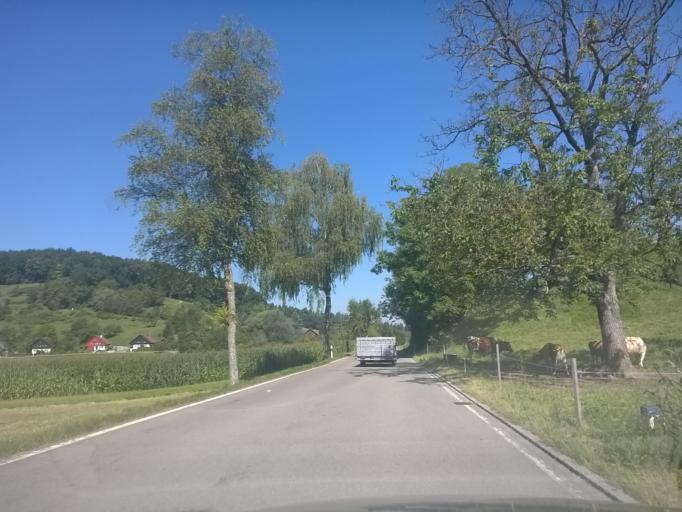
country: CH
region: Zurich
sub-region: Bezirk Winterthur
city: Wuelflingen (Kreis 6) / Niederfeld
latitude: 47.4980
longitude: 8.6731
